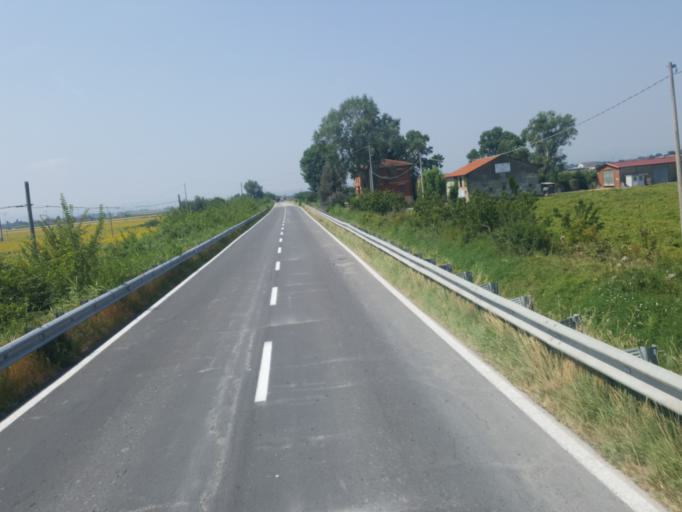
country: IT
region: Emilia-Romagna
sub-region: Provincia di Bologna
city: Sesto Imolese
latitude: 44.4648
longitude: 11.7639
